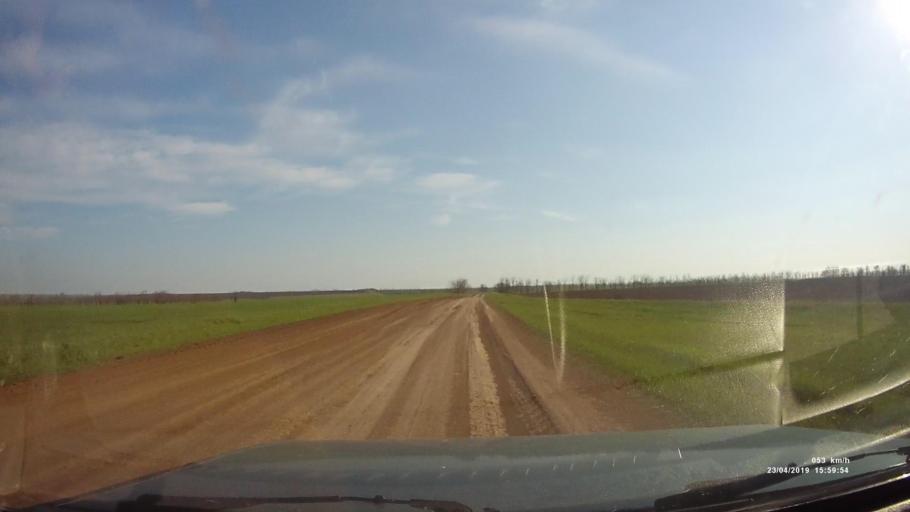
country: RU
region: Rostov
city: Remontnoye
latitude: 46.5129
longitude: 43.1090
